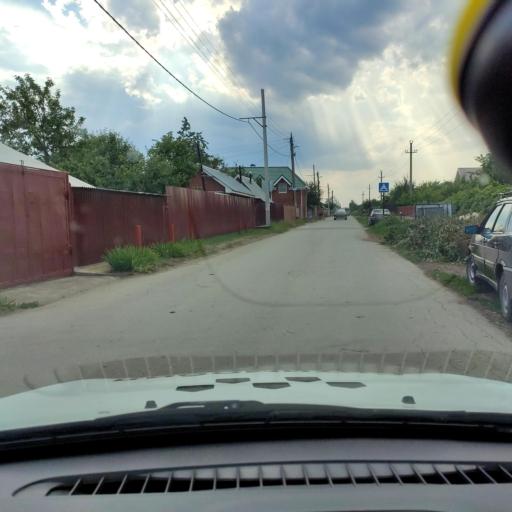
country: RU
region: Samara
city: Podstepki
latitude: 53.5074
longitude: 49.1345
